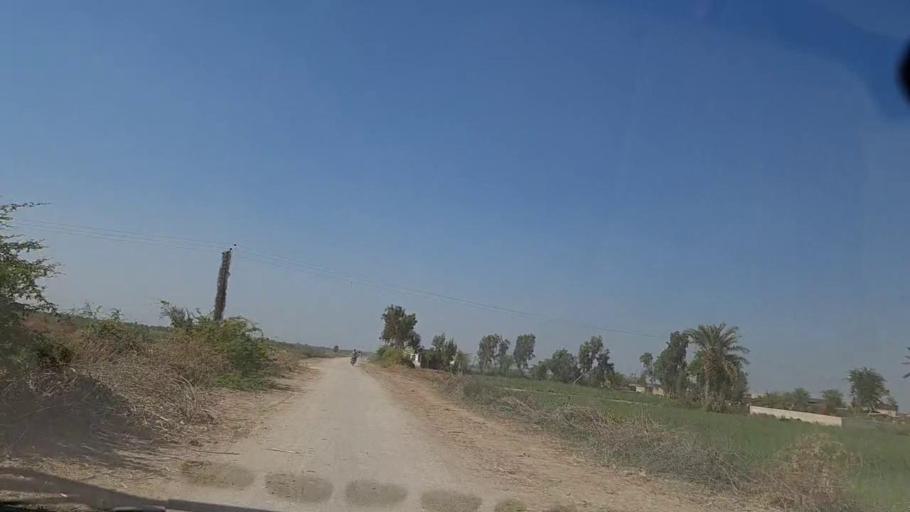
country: PK
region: Sindh
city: Mirwah Gorchani
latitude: 25.3689
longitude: 68.9910
